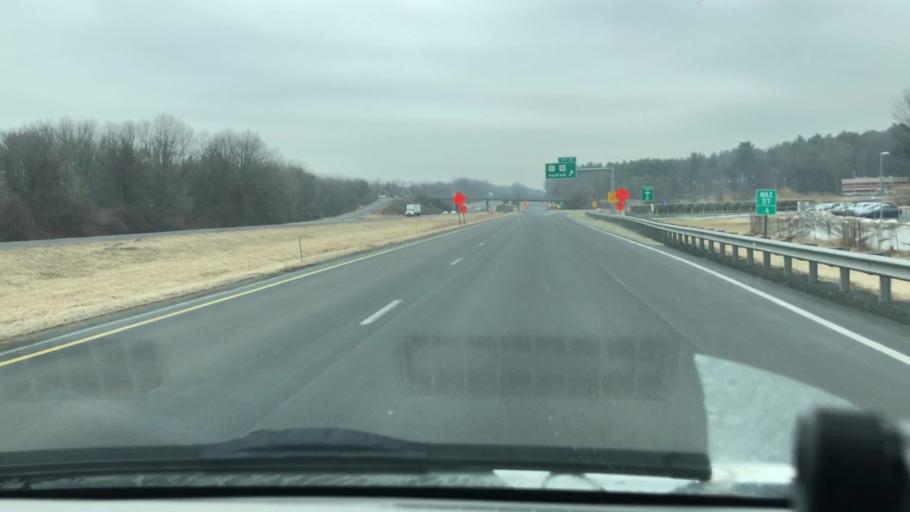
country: US
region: Massachusetts
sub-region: Hampshire County
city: Hatfield
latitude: 42.3652
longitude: -72.6355
